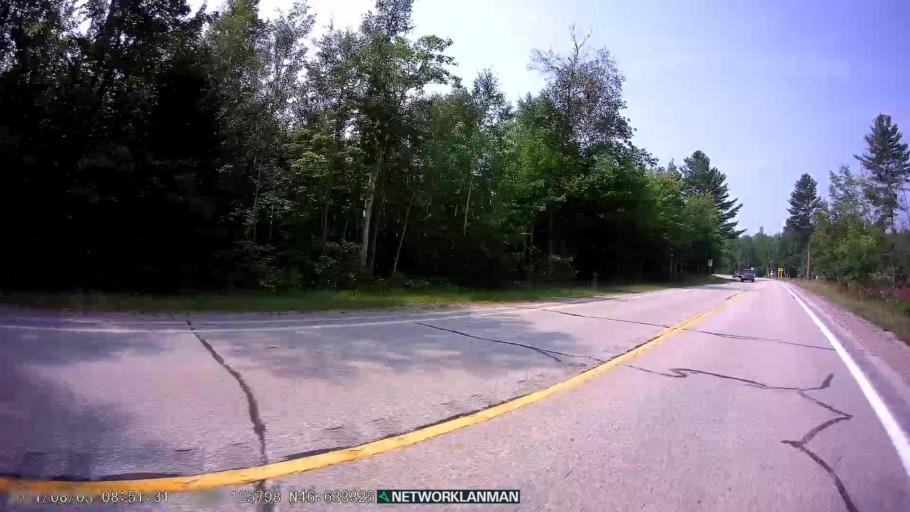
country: US
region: Michigan
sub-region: Luce County
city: Newberry
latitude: 46.6332
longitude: -85.1270
